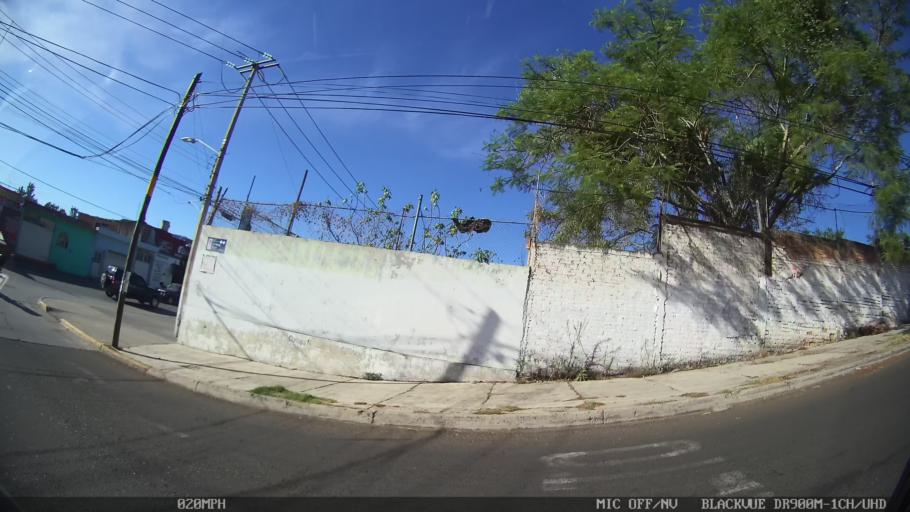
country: MX
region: Jalisco
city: Tlaquepaque
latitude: 20.6786
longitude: -103.2680
